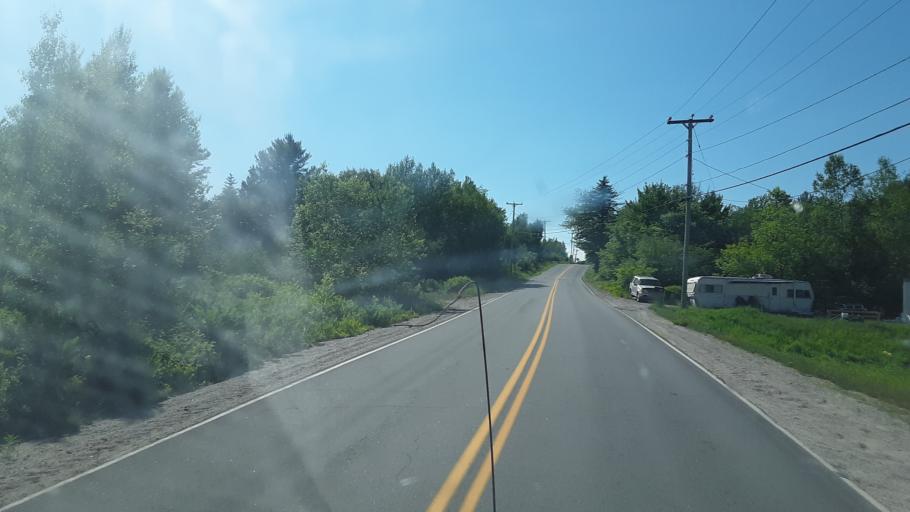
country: US
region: Maine
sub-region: Washington County
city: Cherryfield
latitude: 44.6177
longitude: -67.9264
